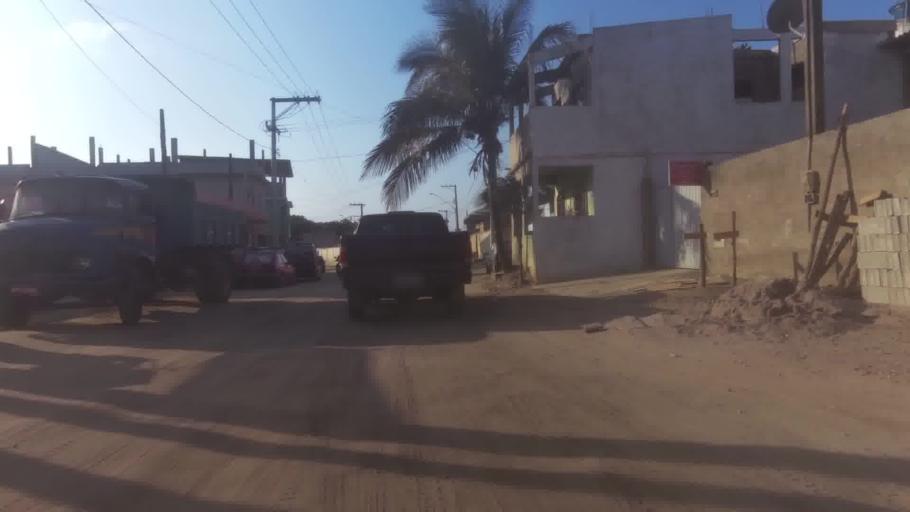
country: BR
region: Espirito Santo
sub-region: Itapemirim
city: Itapemirim
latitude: -21.0222
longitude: -40.8215
